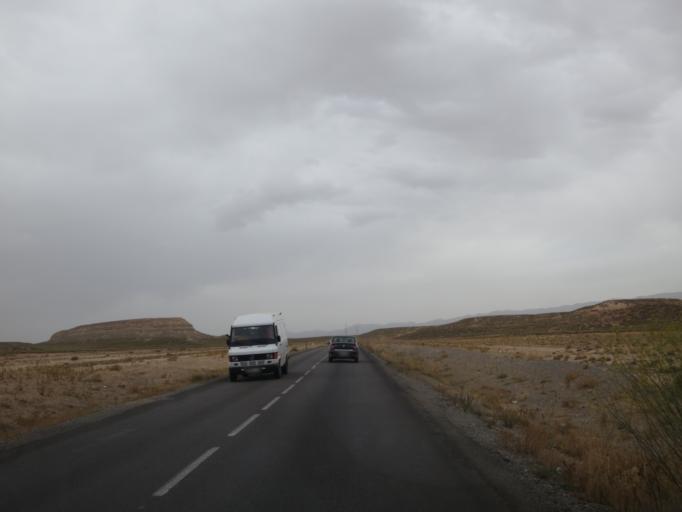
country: MA
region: Meknes-Tafilalet
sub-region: Khenifra
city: Midelt
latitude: 32.7288
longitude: -4.8994
